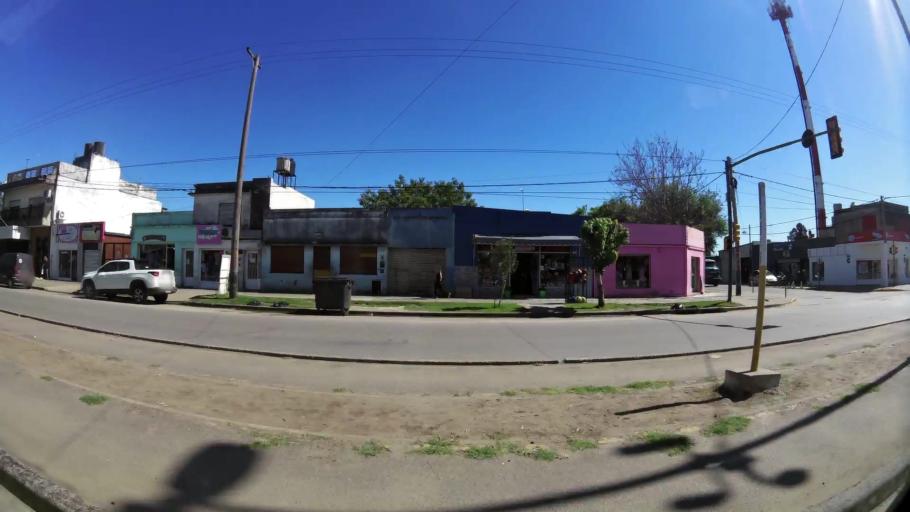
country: AR
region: Santa Fe
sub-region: Departamento de Rosario
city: Rosario
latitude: -32.9705
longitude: -60.6937
